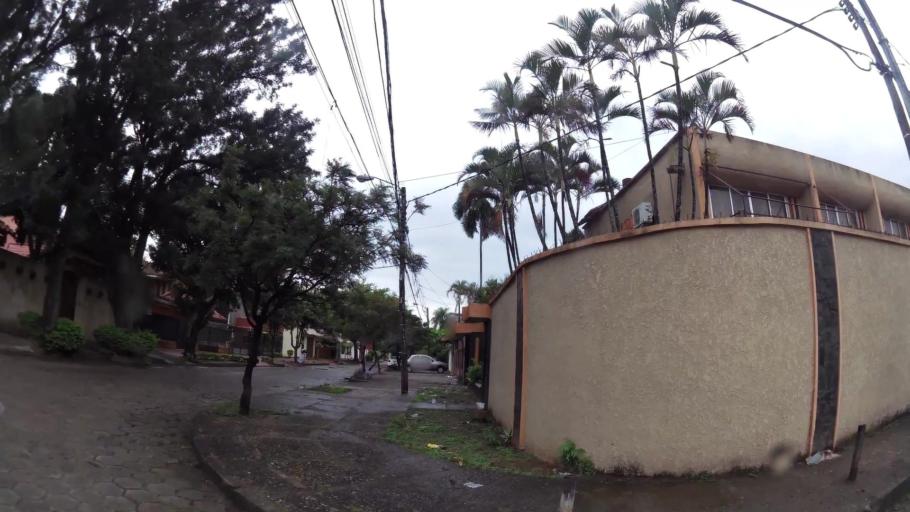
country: BO
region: Santa Cruz
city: Santa Cruz de la Sierra
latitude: -17.7963
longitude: -63.1726
